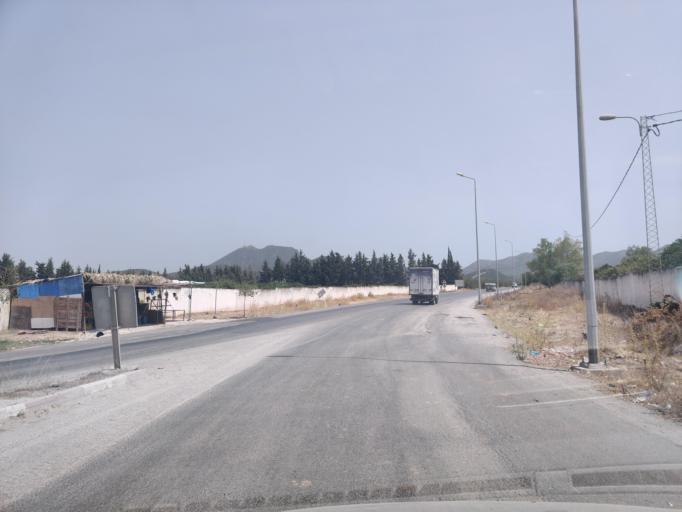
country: TN
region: Tunis
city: La Sebala du Mornag
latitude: 36.6632
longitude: 10.3223
